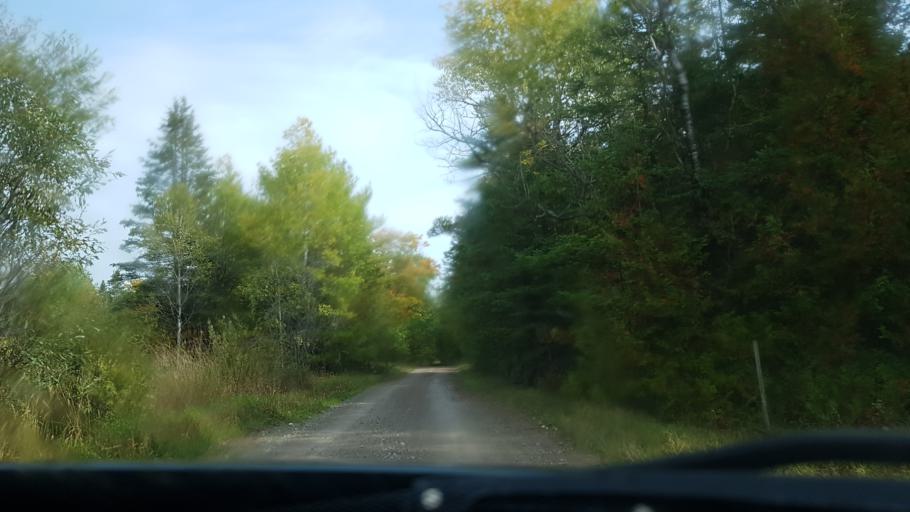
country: CA
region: Ontario
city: Orillia
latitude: 44.6861
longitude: -79.0478
